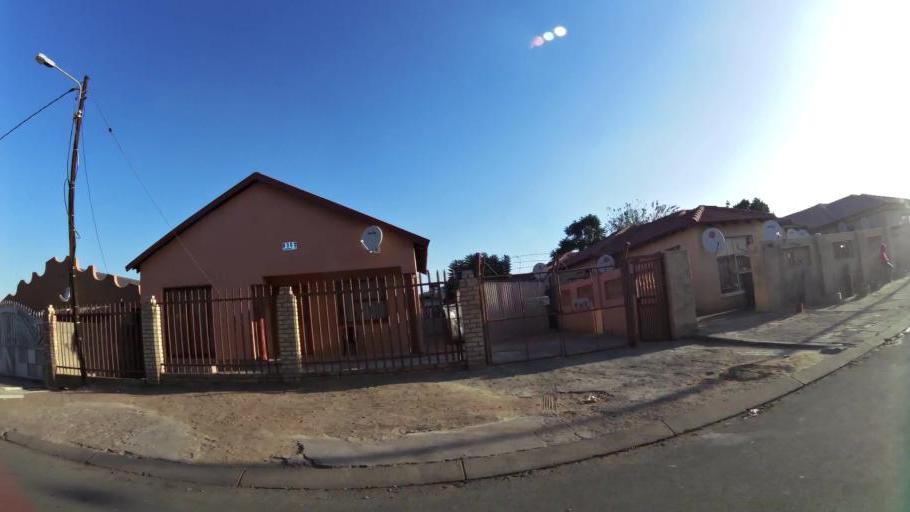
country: ZA
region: North-West
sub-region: Bojanala Platinum District Municipality
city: Rustenburg
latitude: -25.6449
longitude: 27.2157
